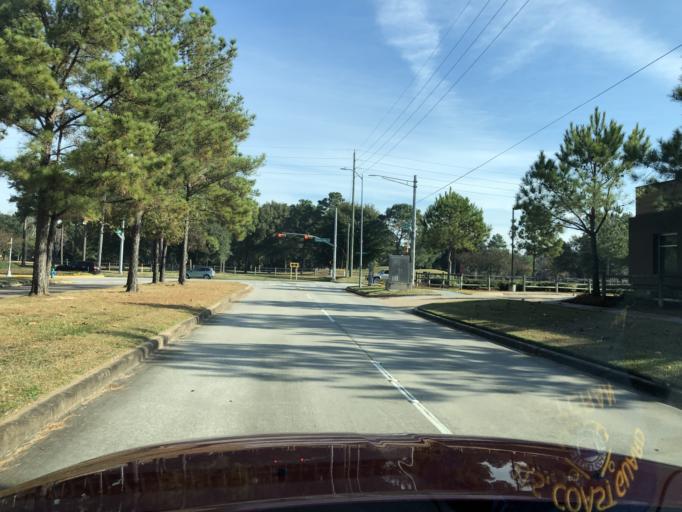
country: US
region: Texas
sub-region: Harris County
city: Tomball
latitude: 30.0365
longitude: -95.5618
